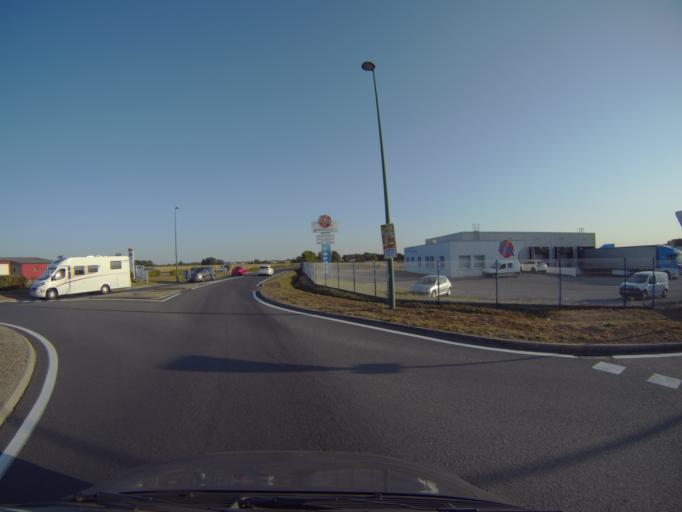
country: FR
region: Pays de la Loire
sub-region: Departement de la Vendee
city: Cugand
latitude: 47.0557
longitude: -1.2542
